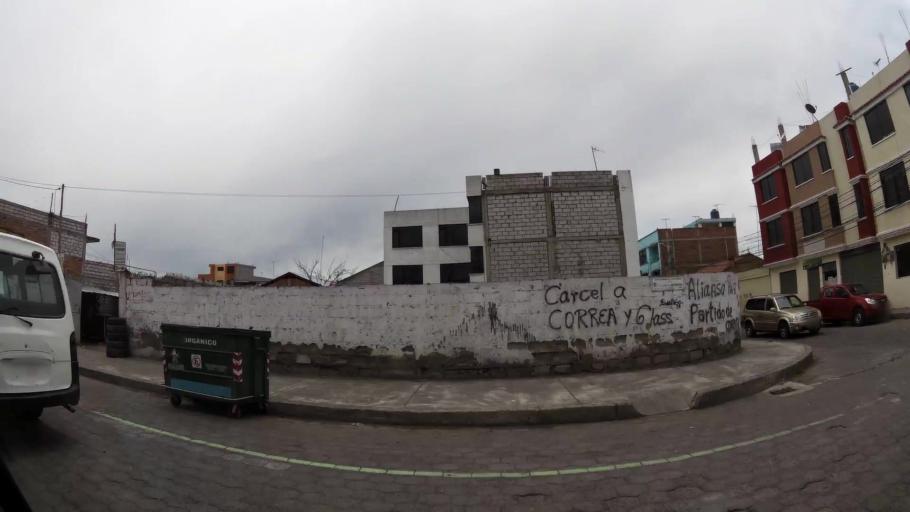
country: EC
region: Cotopaxi
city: San Miguel de Salcedo
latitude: -1.0413
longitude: -78.5867
